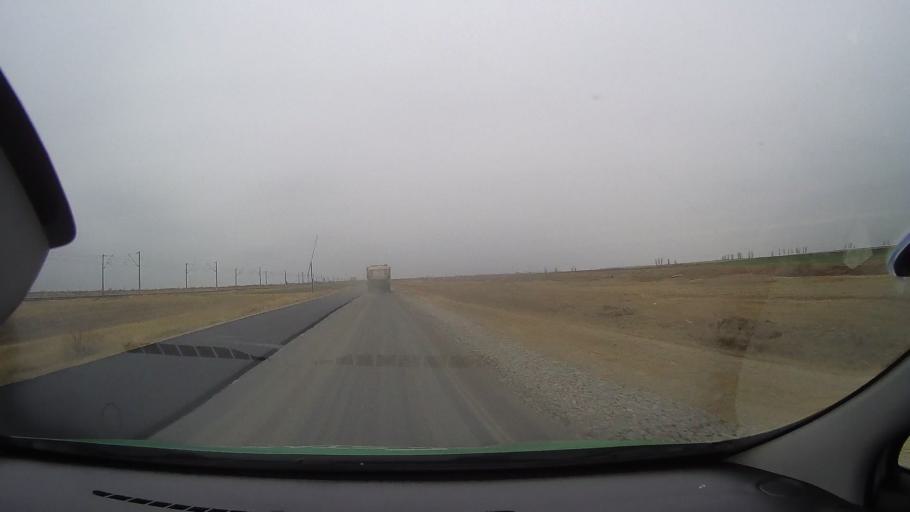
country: RO
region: Braila
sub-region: Comuna Baraganul
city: Baraganul
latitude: 44.7967
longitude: 27.5307
